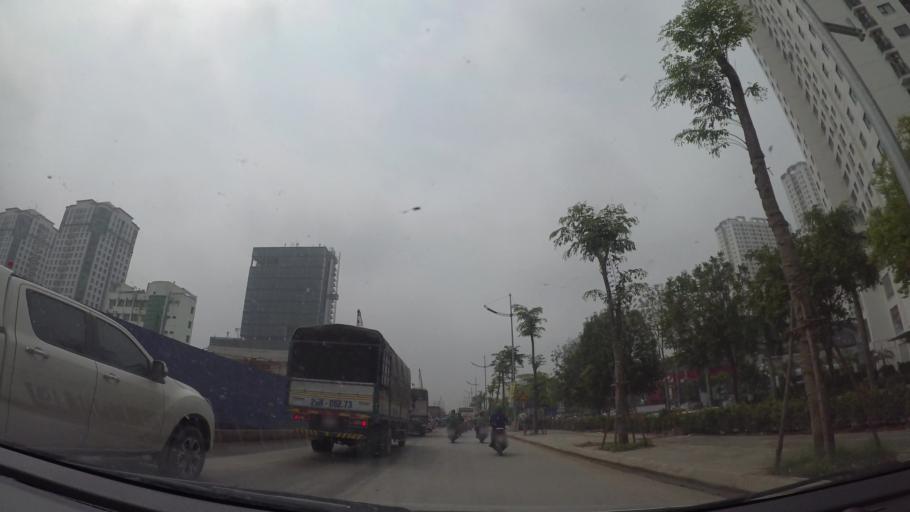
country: VN
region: Ha Noi
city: Cau Dien
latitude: 21.0519
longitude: 105.7814
